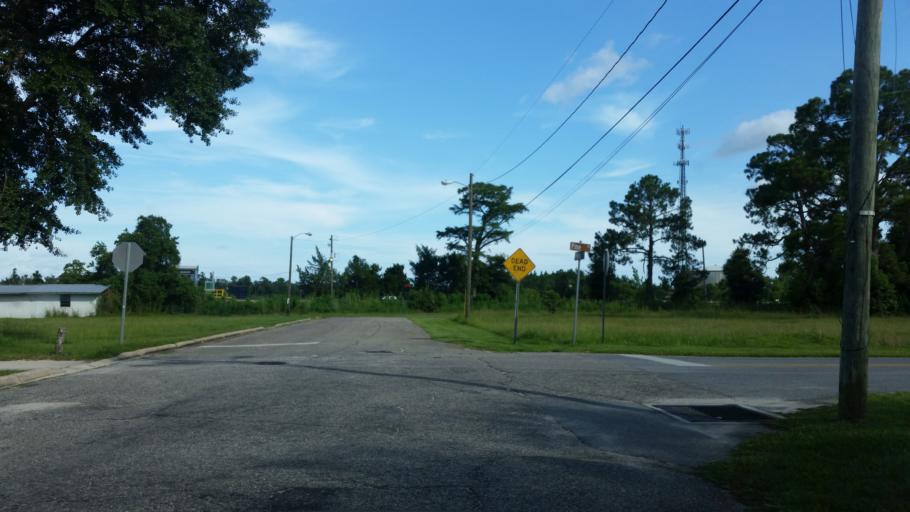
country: US
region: Florida
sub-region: Santa Rosa County
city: Milton
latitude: 30.6217
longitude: -87.0347
